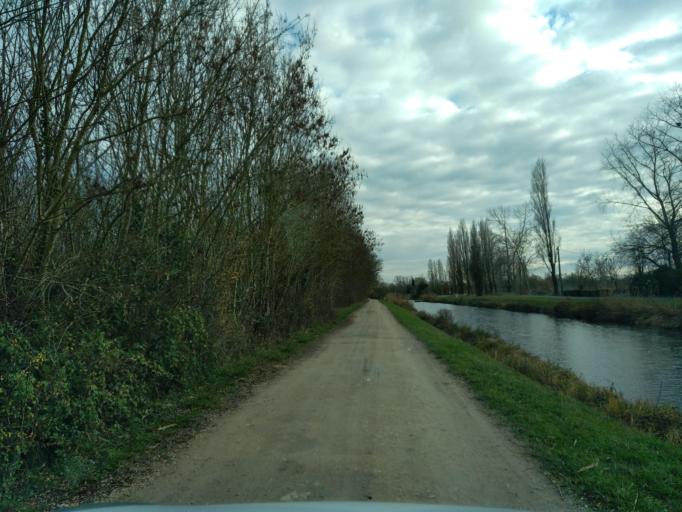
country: FR
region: Pays de la Loire
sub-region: Departement de la Vendee
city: Maillezais
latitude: 46.3158
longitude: -0.7745
